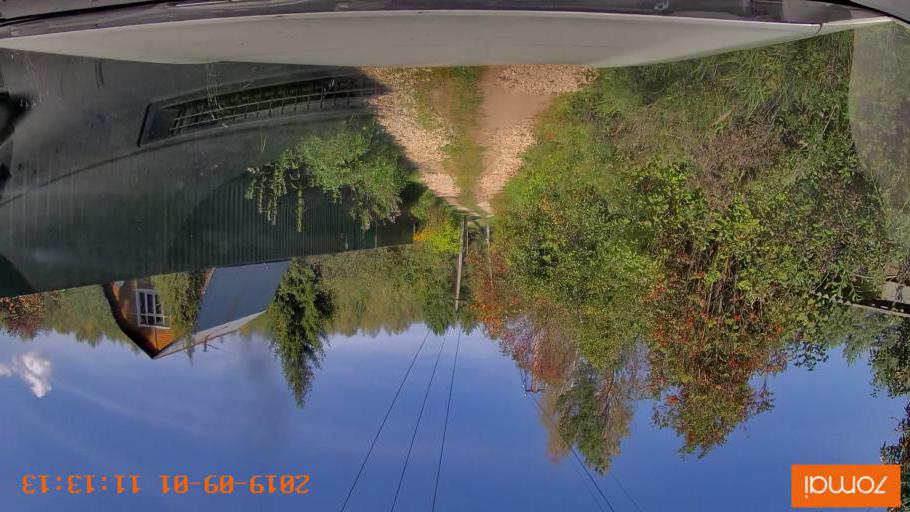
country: RU
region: Kaluga
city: Detchino
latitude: 54.8210
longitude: 36.3719
